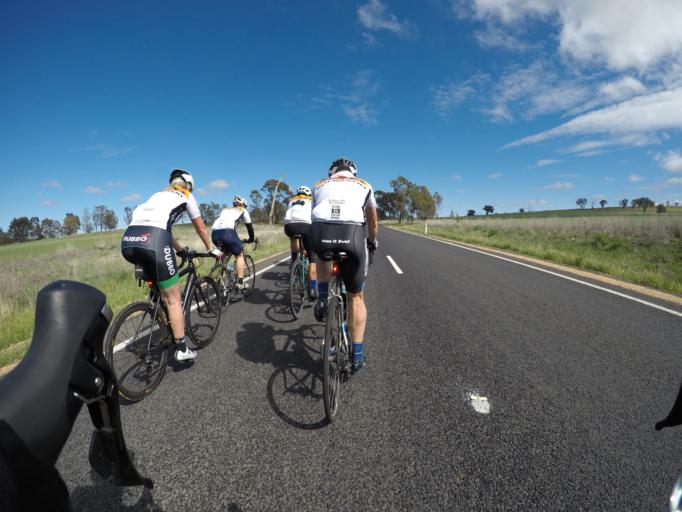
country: AU
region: New South Wales
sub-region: Wellington
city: Wellington
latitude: -32.7427
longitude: 148.5964
